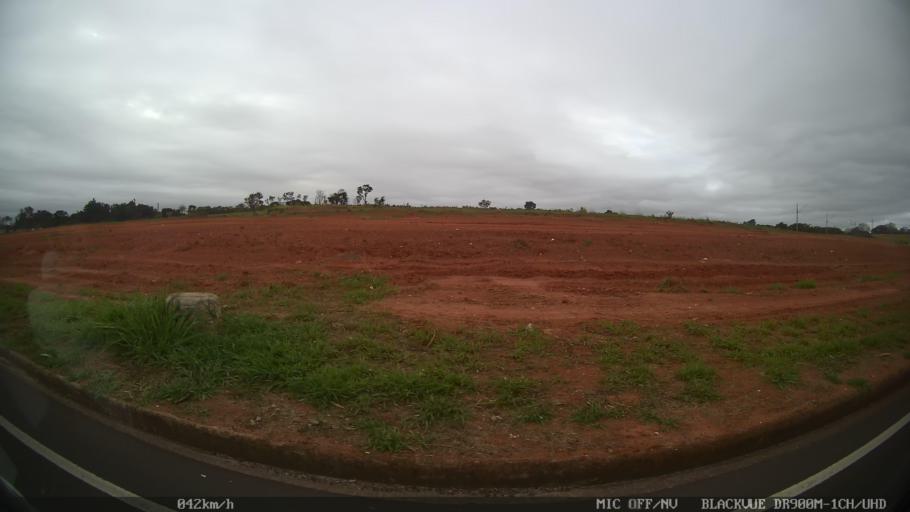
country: BR
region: Sao Paulo
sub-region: Sao Jose Do Rio Preto
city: Sao Jose do Rio Preto
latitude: -20.8226
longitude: -49.4369
